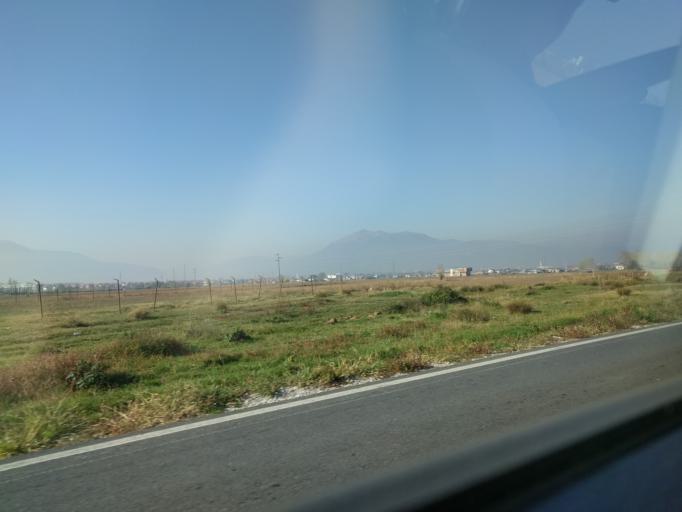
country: XK
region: Prizren
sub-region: Prizren
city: Prizren
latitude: 42.2390
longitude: 20.7561
